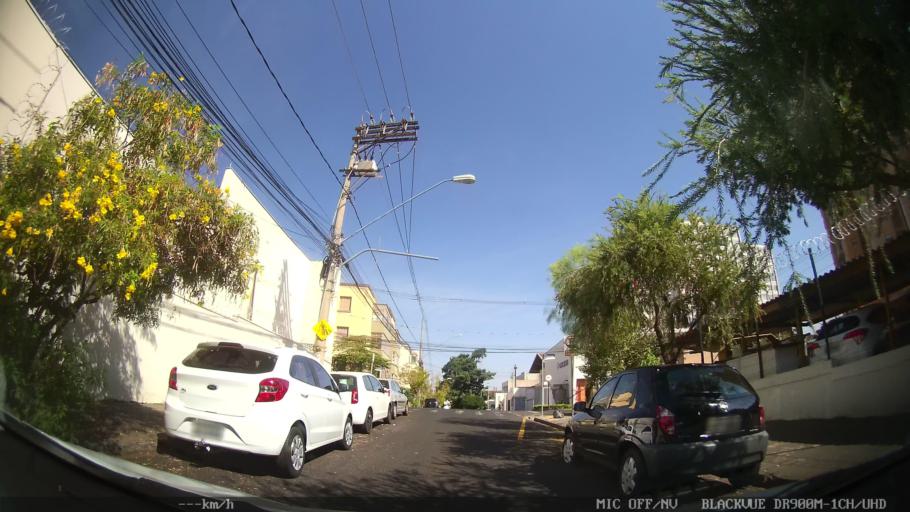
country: BR
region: Sao Paulo
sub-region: Ribeirao Preto
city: Ribeirao Preto
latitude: -21.1802
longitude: -47.8146
